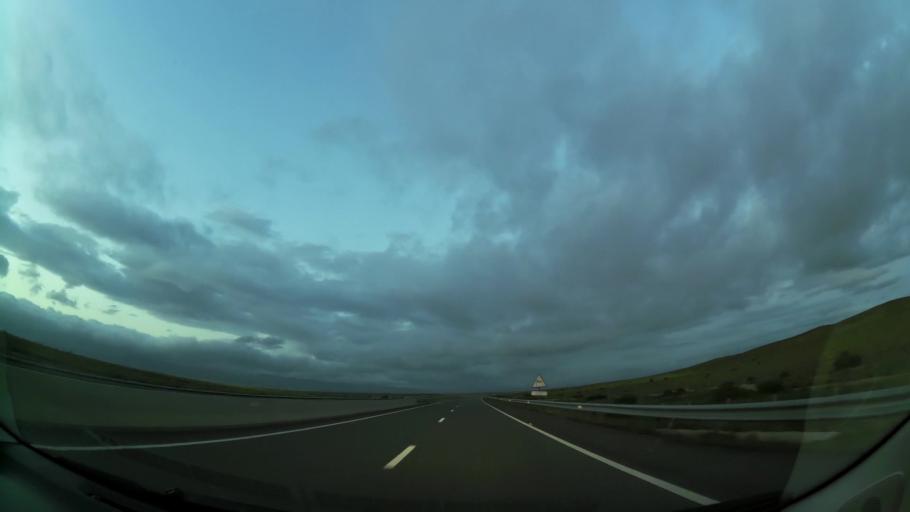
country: MA
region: Oriental
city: El Aioun
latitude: 34.6234
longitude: -2.3953
